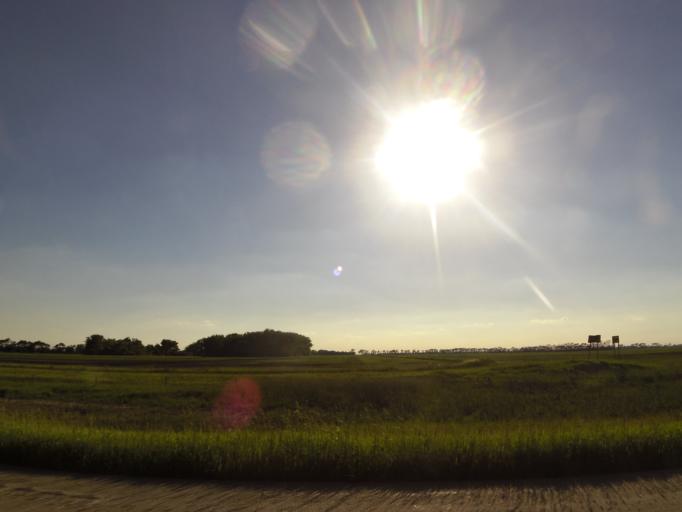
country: US
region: North Dakota
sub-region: Grand Forks County
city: Grand Forks
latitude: 48.1499
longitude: -97.1909
